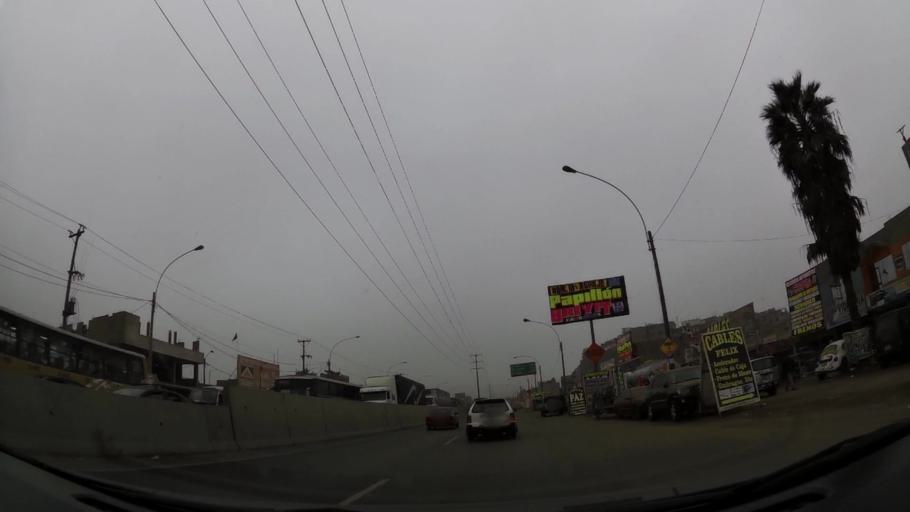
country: PE
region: Lima
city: Ventanilla
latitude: -11.8492
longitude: -77.0941
